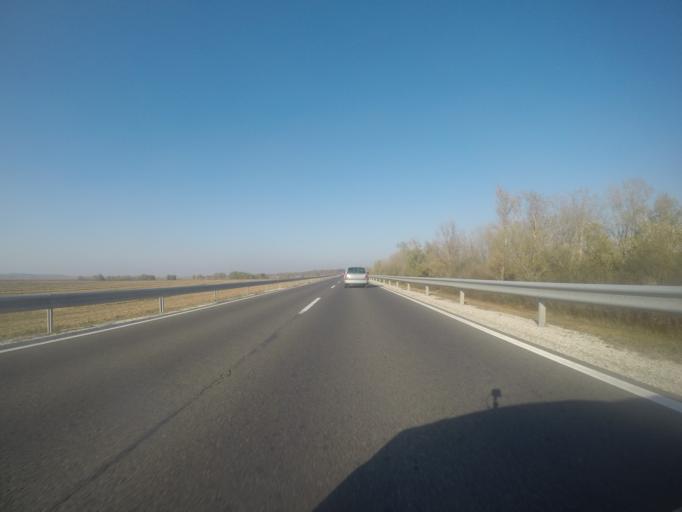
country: HU
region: Fejer
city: Adony
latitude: 47.1590
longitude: 18.8621
